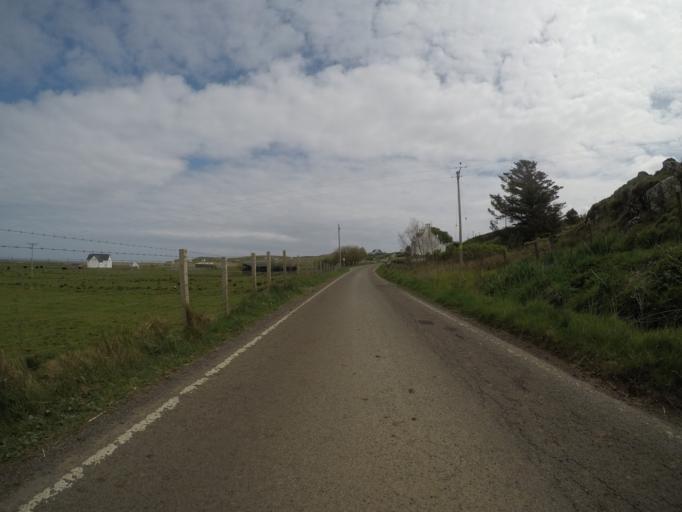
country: GB
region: Scotland
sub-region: Highland
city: Portree
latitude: 57.6847
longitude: -6.3077
